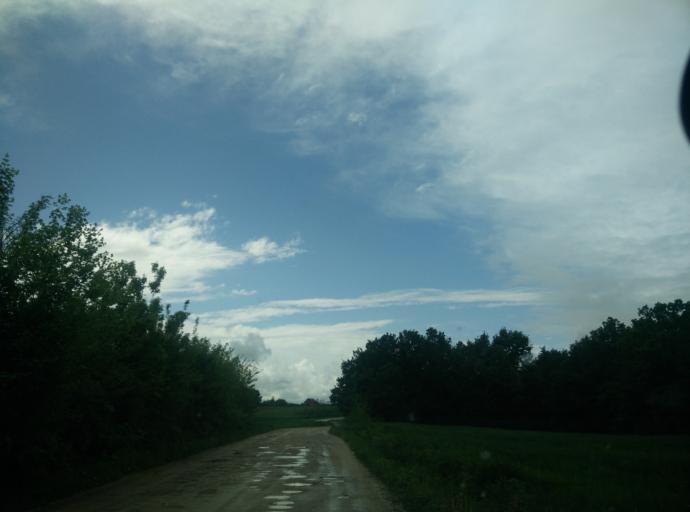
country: BA
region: Brcko
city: Brcko
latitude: 44.7835
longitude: 18.8214
